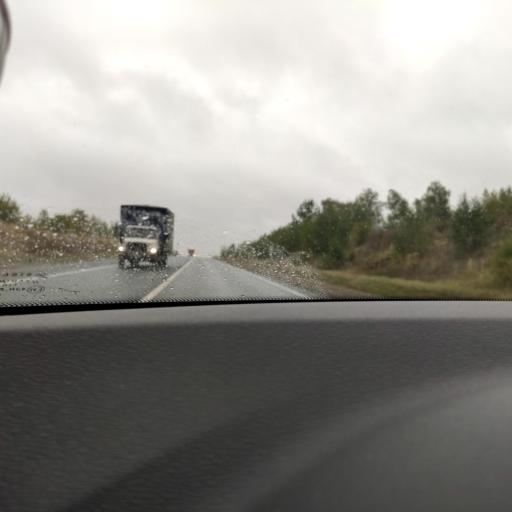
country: RU
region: Samara
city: Mirnyy
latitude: 53.6429
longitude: 50.2222
